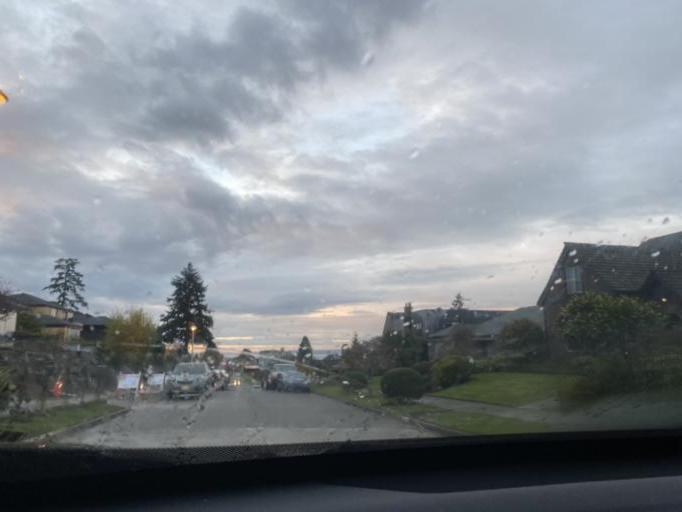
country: US
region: Washington
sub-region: King County
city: Seattle
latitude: 47.6460
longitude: -122.4109
